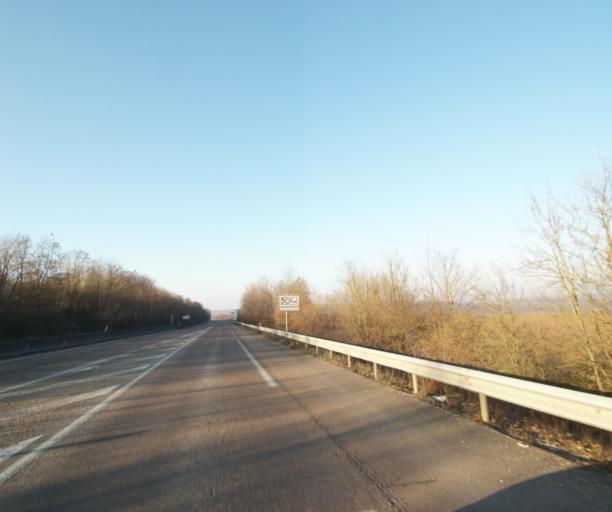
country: FR
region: Champagne-Ardenne
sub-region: Departement de la Haute-Marne
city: Chevillon
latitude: 48.5353
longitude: 5.0901
